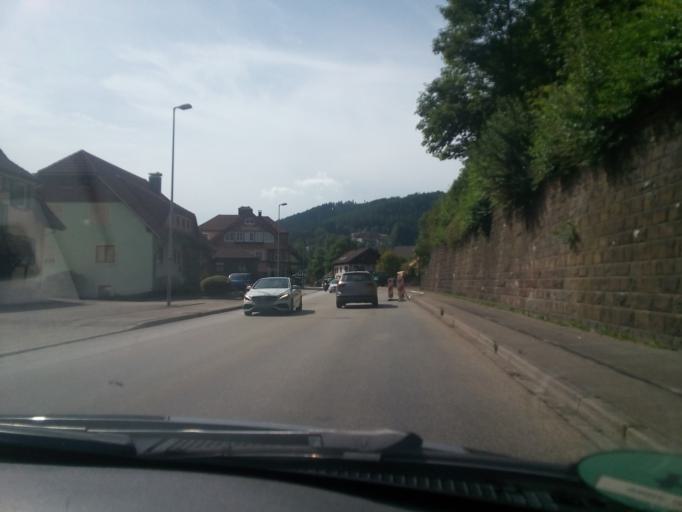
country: DE
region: Baden-Wuerttemberg
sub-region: Karlsruhe Region
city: Biberach
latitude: 48.5332
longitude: 8.2939
